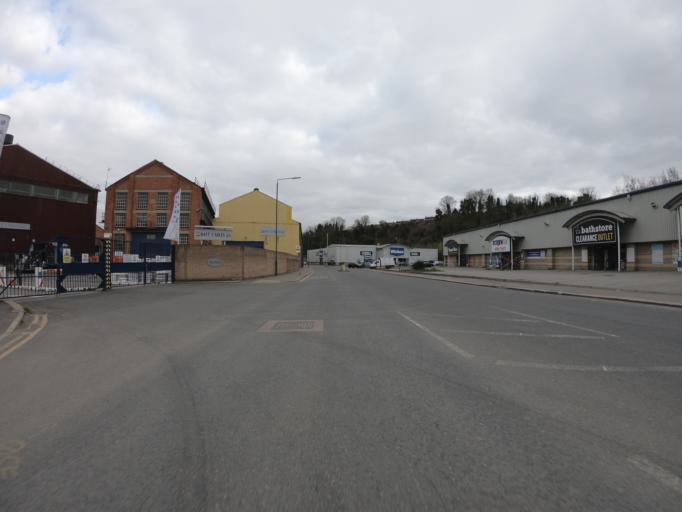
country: GB
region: England
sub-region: Greater London
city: Erith
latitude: 51.4824
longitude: 0.1672
